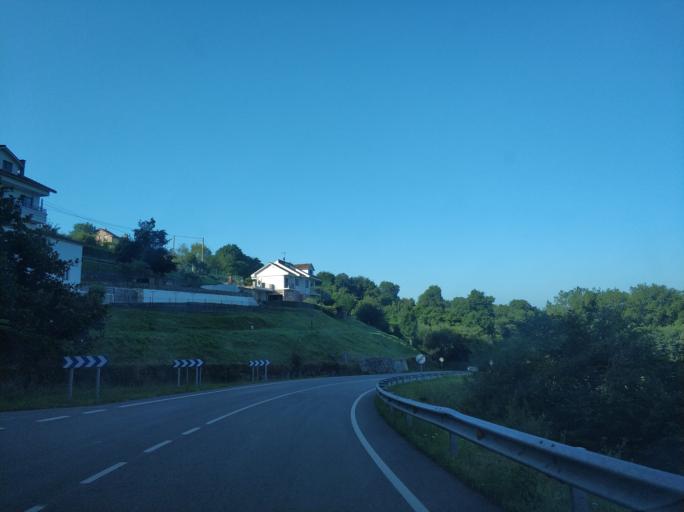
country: ES
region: Cantabria
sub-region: Provincia de Cantabria
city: Camargo
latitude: 43.3983
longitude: -3.9423
